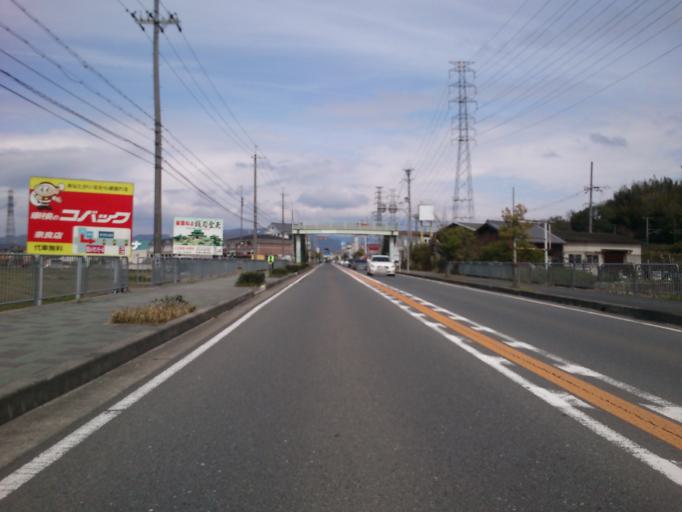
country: JP
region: Nara
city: Nara-shi
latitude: 34.7237
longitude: 135.8177
